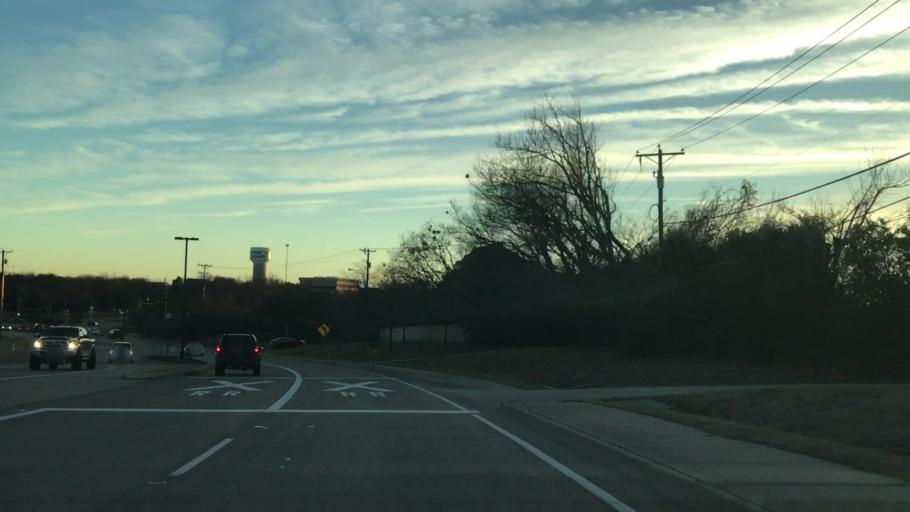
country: US
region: Texas
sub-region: Rockwall County
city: Rockwall
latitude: 32.9081
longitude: -96.4638
